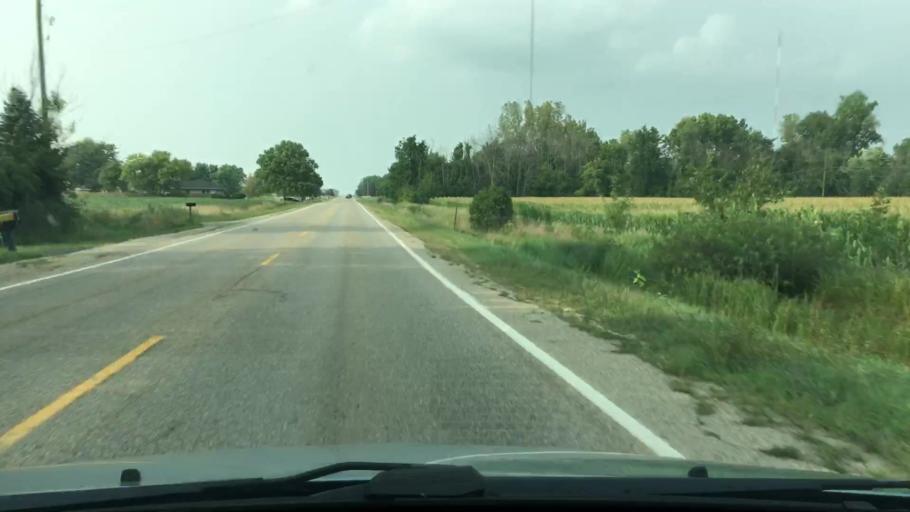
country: US
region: Michigan
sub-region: Ottawa County
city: Allendale
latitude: 42.9470
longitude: -85.9036
